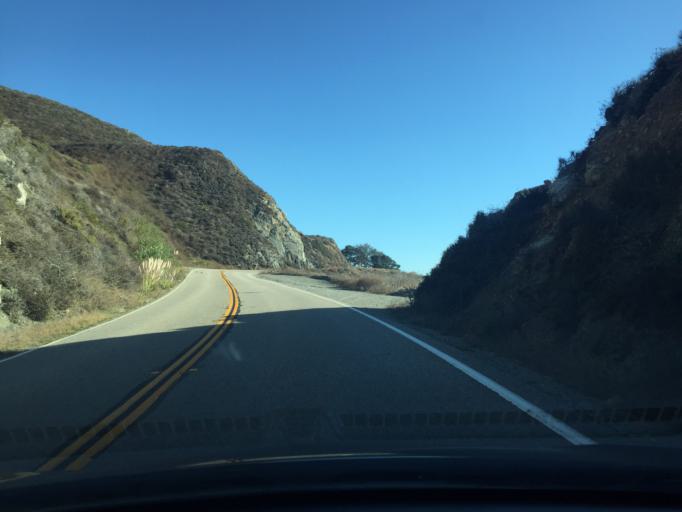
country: US
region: California
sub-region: Monterey County
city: King City
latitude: 35.8892
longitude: -121.4611
